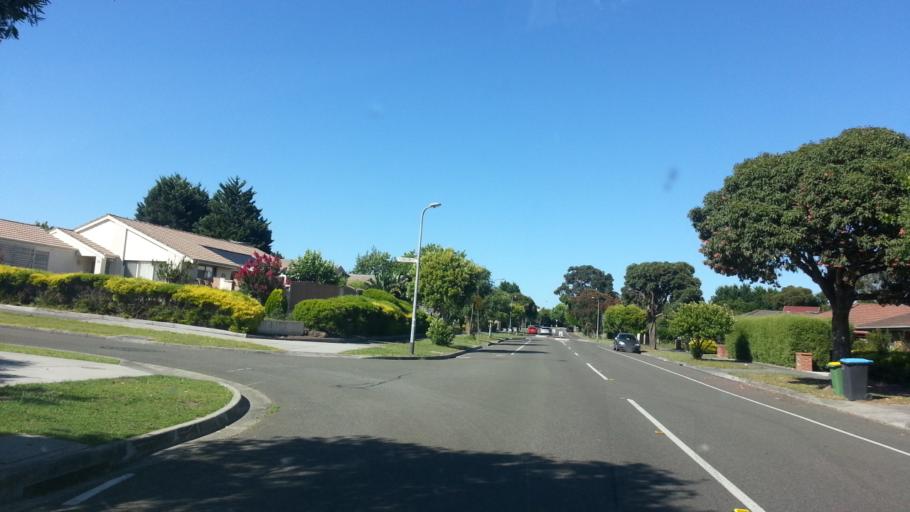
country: AU
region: Victoria
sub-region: Yarra Ranges
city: Lysterfield
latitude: -37.9239
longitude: 145.2675
